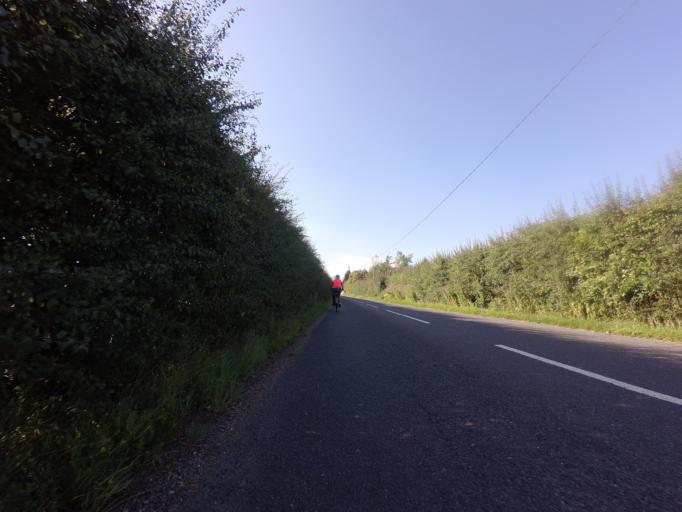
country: GB
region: England
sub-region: Kent
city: Tenterden
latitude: 51.0517
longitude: 0.6936
